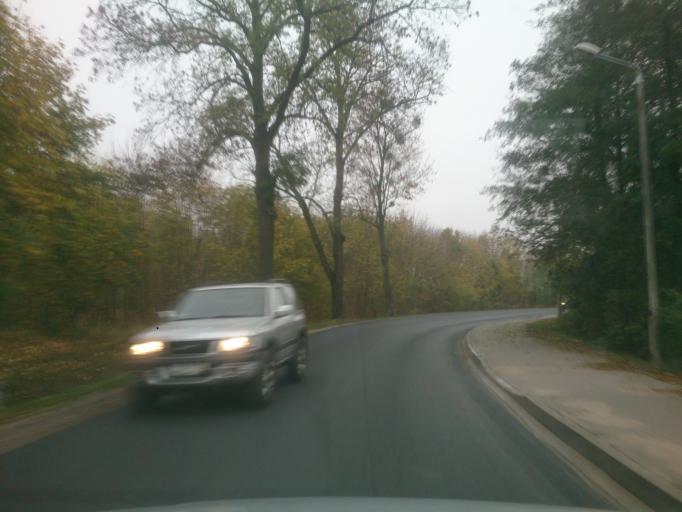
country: PL
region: Kujawsko-Pomorskie
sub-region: Powiat brodnicki
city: Brodnica
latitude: 53.2737
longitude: 19.3901
